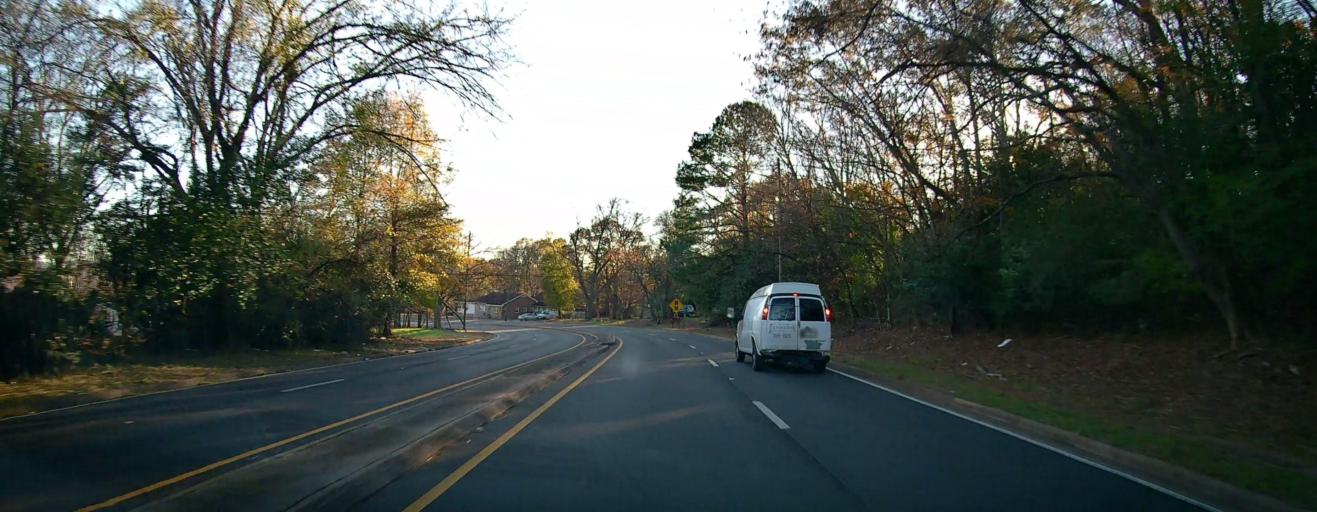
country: US
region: Alabama
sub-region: Jefferson County
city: Birmingham
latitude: 33.5596
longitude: -86.8201
